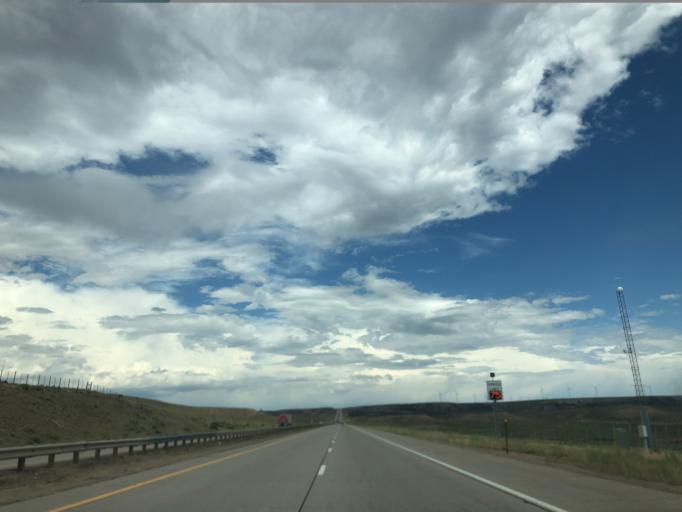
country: US
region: Wyoming
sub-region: Uinta County
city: Mountain View
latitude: 41.2983
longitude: -110.6173
